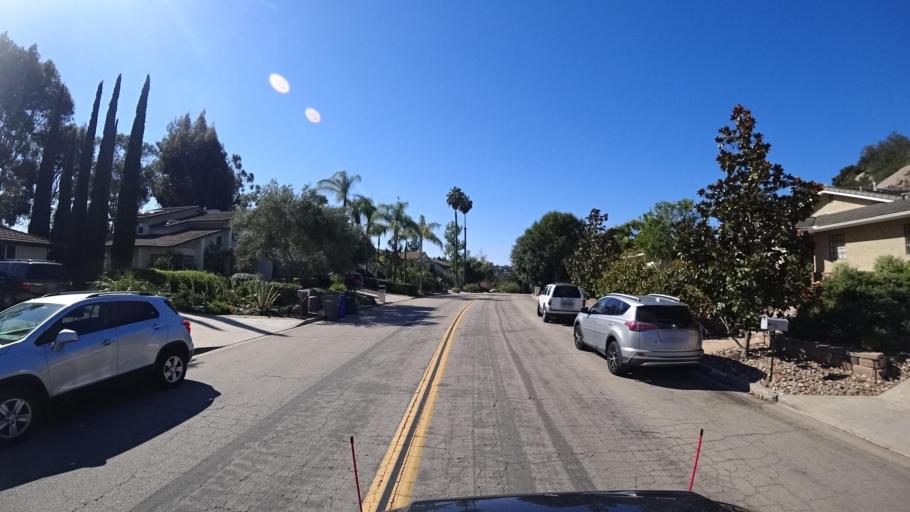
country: US
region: California
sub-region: San Diego County
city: Hidden Meadows
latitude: 33.2209
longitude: -117.1176
